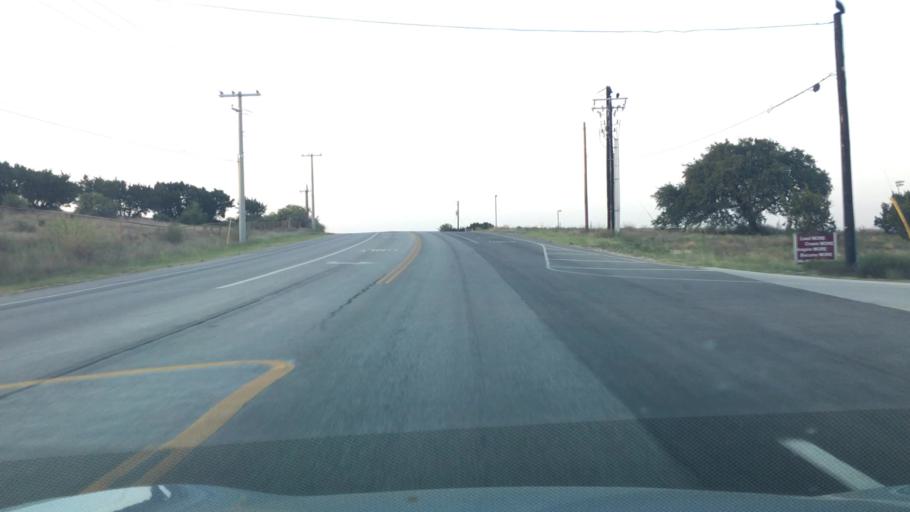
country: US
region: Texas
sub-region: Hays County
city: Dripping Springs
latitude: 30.1788
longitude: -98.0022
